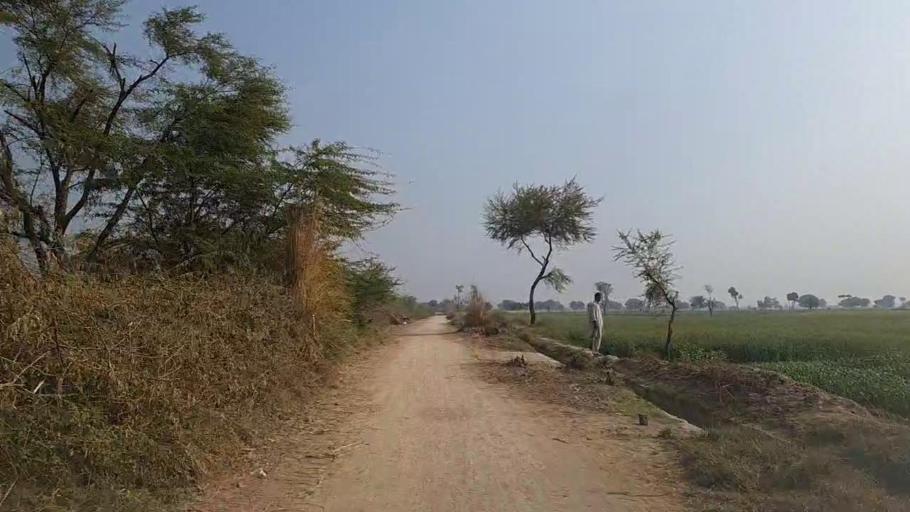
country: PK
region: Sindh
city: Nawabshah
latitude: 26.2882
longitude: 68.4445
